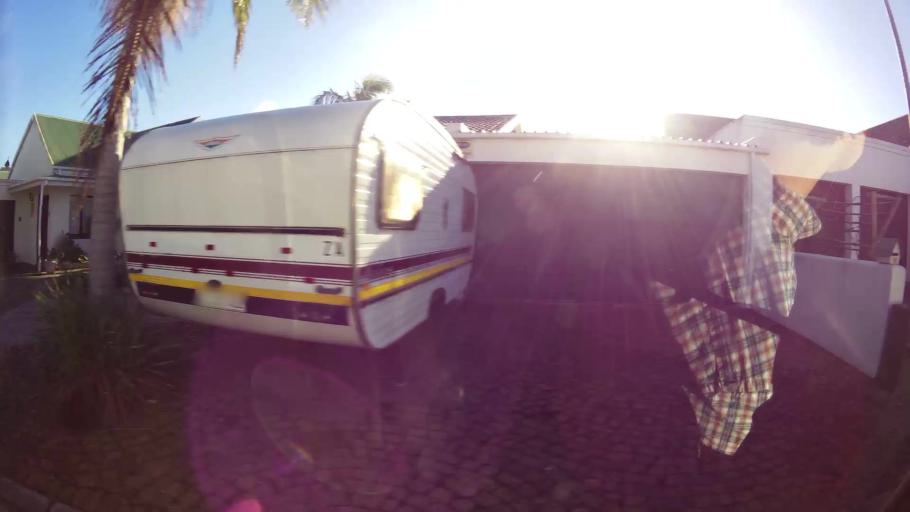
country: ZA
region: Western Cape
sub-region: Eden District Municipality
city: George
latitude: -33.9607
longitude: 22.4451
